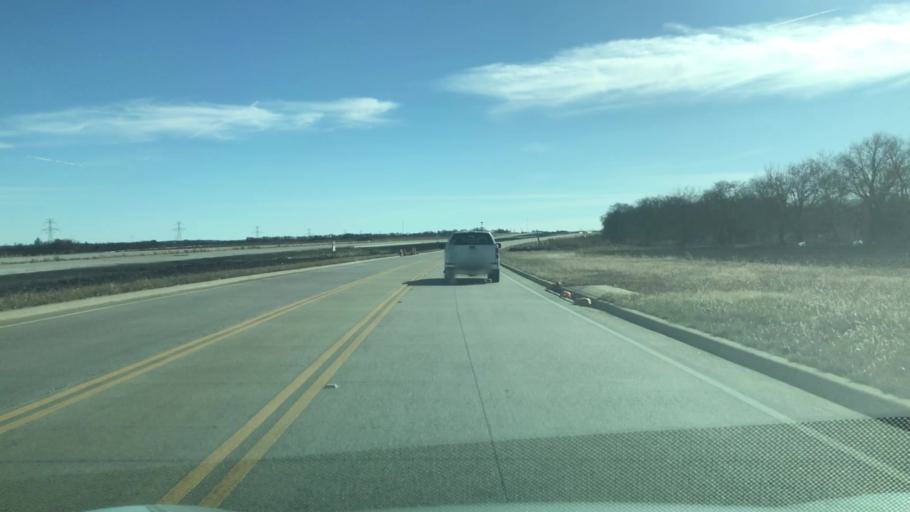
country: US
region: Texas
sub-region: Tarrant County
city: Mansfield
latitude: 32.5405
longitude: -97.0823
